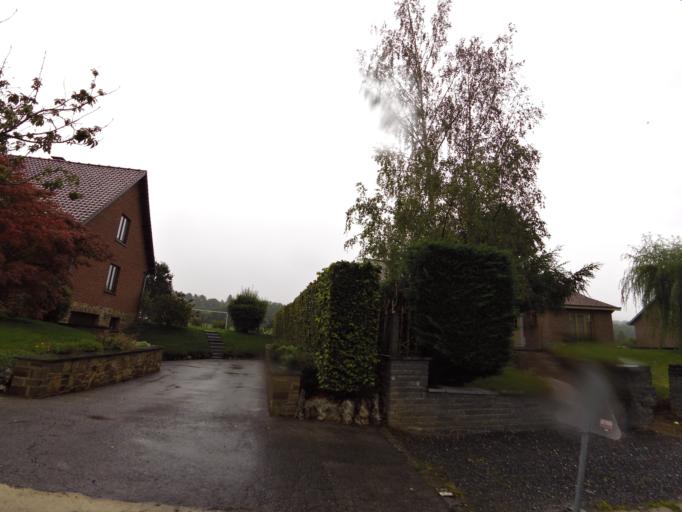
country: BE
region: Wallonia
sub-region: Province de Namur
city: Rochefort
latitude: 50.1620
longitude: 5.2287
